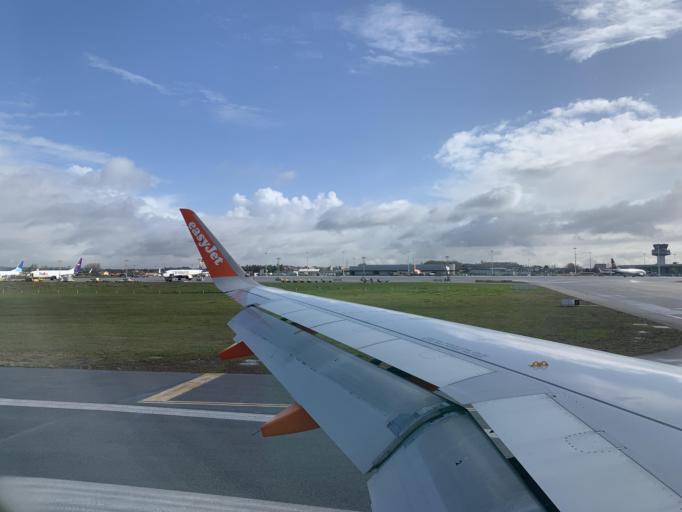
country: PT
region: Porto
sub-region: Matosinhos
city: Santa Cruz do Bispo
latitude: 41.2392
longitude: -8.6787
